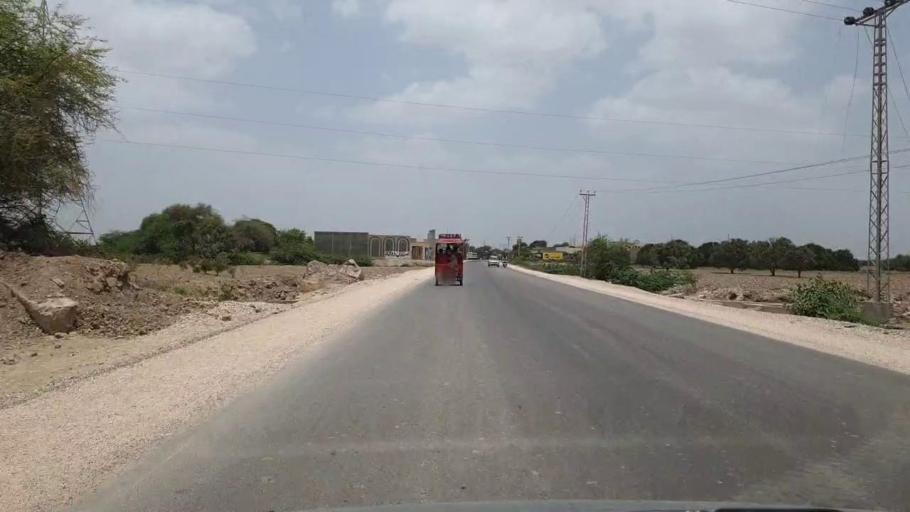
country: PK
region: Sindh
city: Naukot
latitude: 24.8478
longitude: 69.4138
